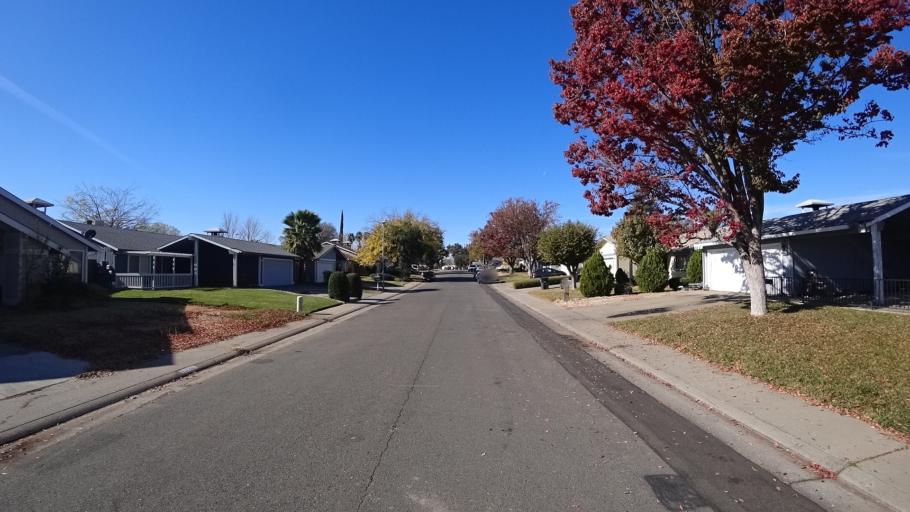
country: US
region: California
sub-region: Sacramento County
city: Antelope
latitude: 38.7193
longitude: -121.3065
